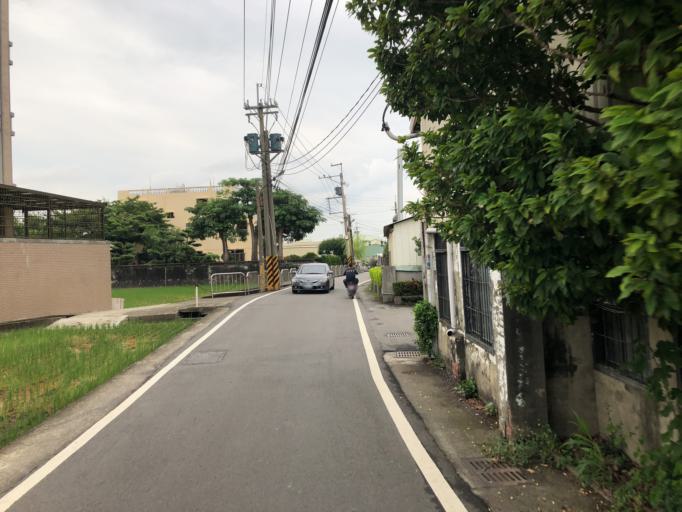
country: TW
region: Taiwan
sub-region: Taichung City
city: Taichung
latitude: 24.0628
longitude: 120.6818
